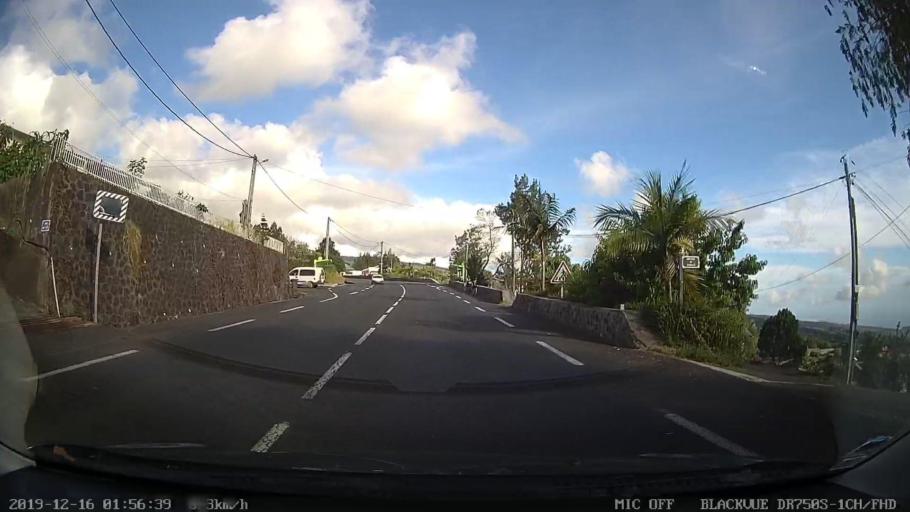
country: RE
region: Reunion
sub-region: Reunion
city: Le Tampon
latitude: -21.2328
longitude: 55.5446
